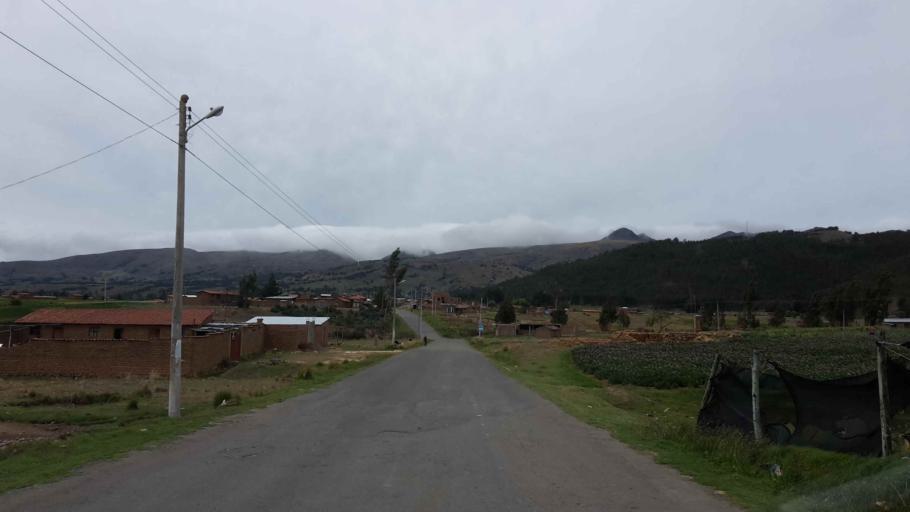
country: BO
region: Cochabamba
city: Arani
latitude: -17.4518
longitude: -65.7195
